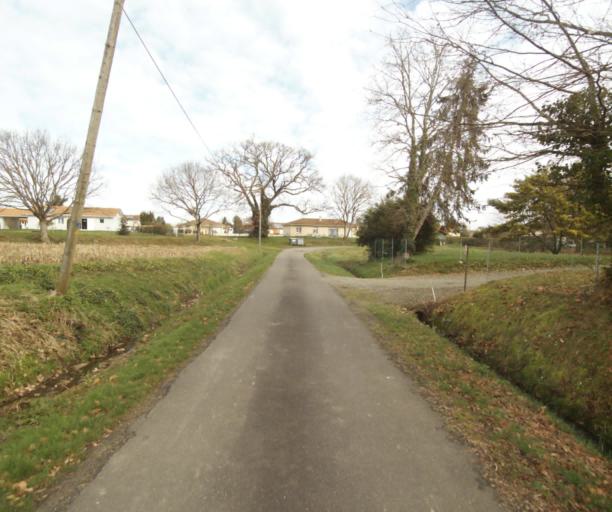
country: FR
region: Aquitaine
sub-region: Departement des Landes
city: Gabarret
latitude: 43.9838
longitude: 0.0047
